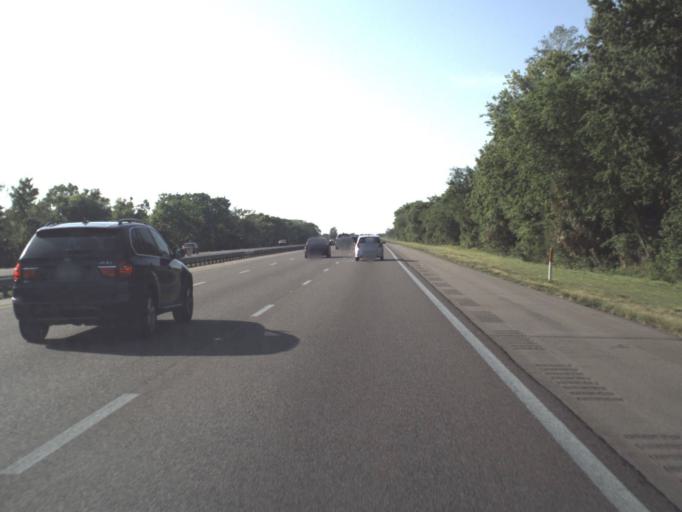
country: US
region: Florida
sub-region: Indian River County
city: Fellsmere
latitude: 27.8443
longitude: -80.5747
